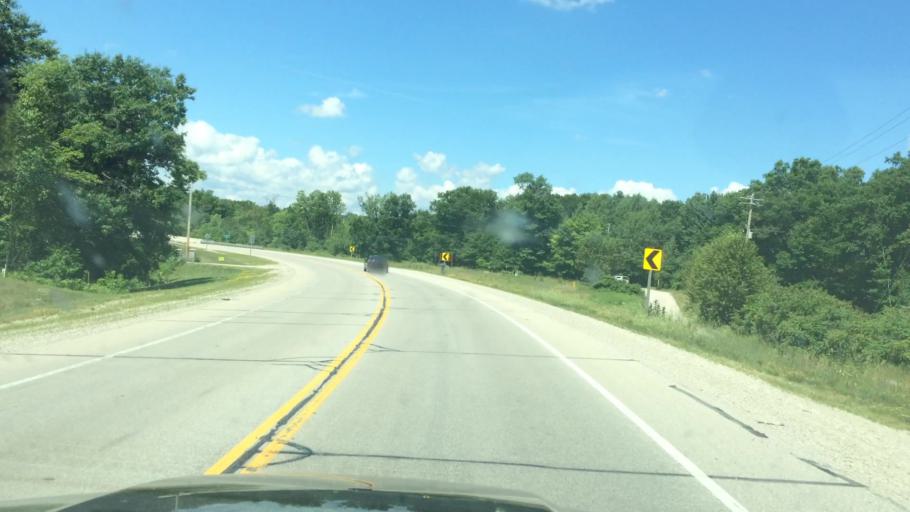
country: US
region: Wisconsin
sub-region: Marinette County
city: Peshtigo
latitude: 45.1059
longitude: -87.7516
